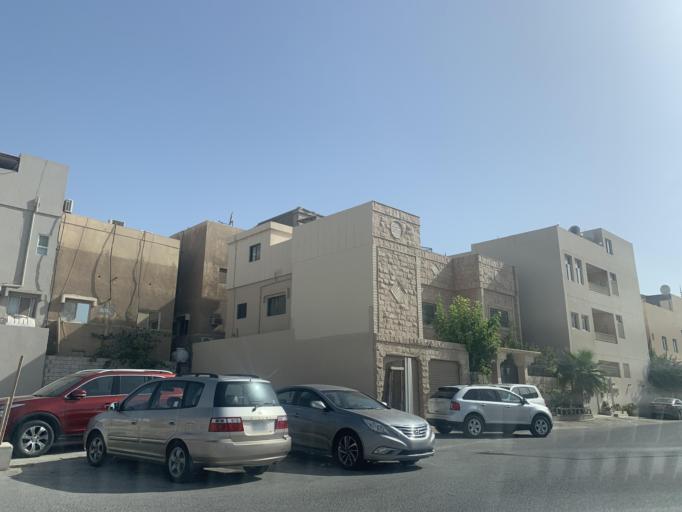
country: BH
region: Manama
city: Jidd Hafs
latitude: 26.2100
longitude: 50.5602
